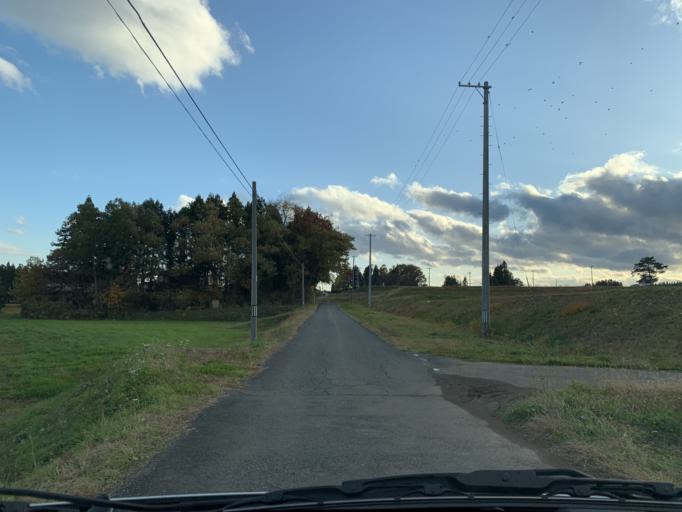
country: JP
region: Iwate
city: Mizusawa
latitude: 39.1048
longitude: 141.0395
